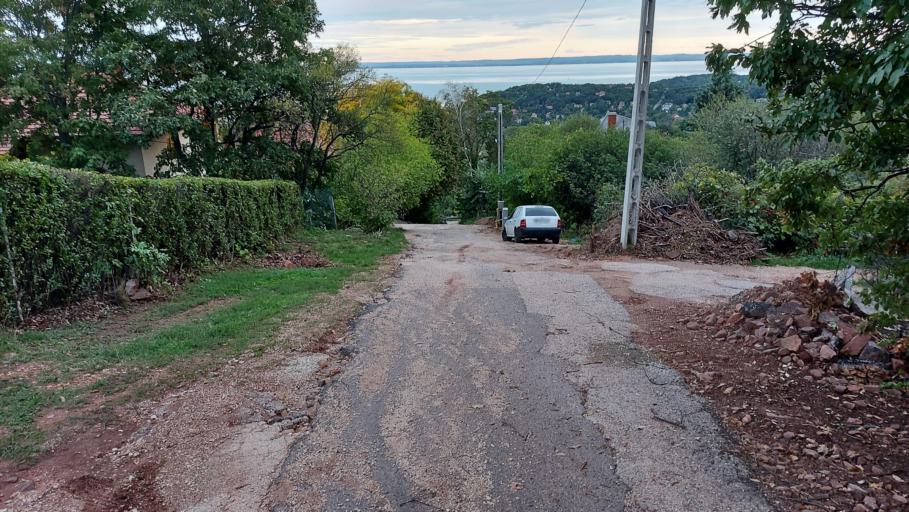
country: HU
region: Veszprem
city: Balatonalmadi
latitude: 47.0269
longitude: 17.9992
